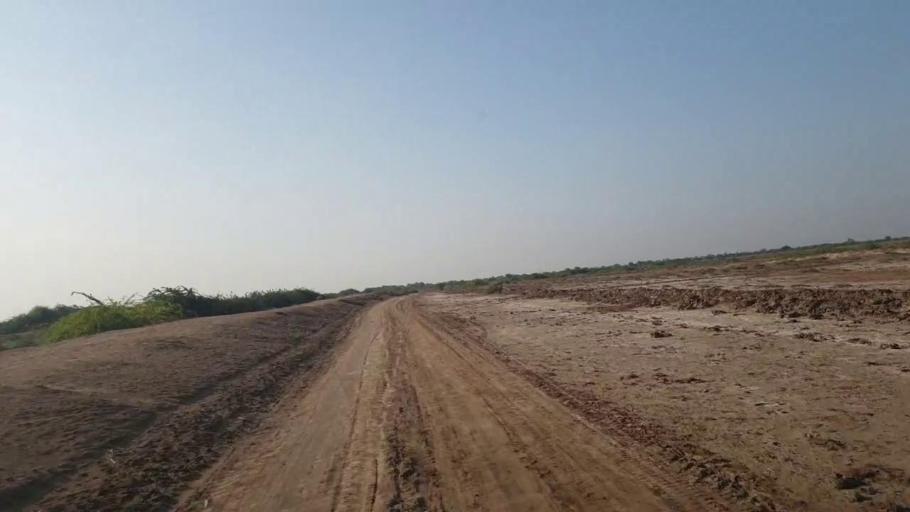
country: PK
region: Sindh
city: Badin
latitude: 24.4649
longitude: 68.7380
